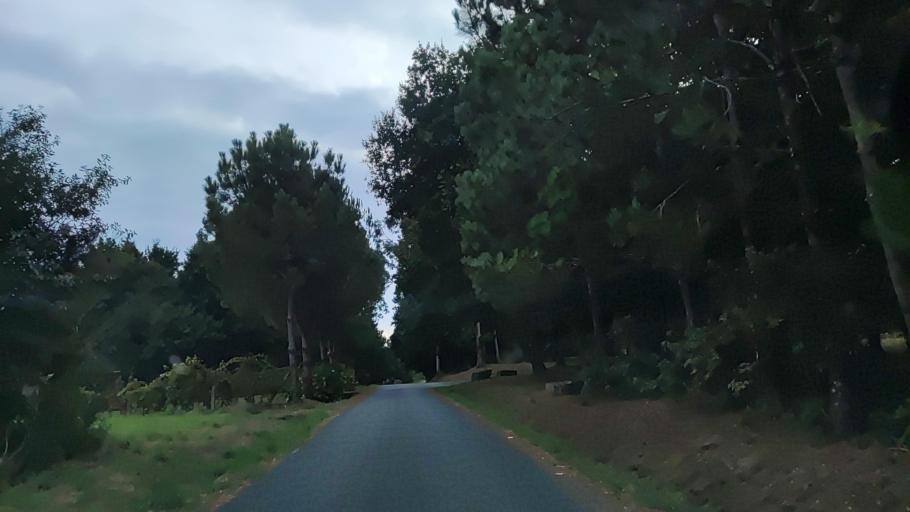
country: ES
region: Galicia
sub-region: Provincia da Coruna
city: Padron
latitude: 42.7149
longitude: -8.6881
